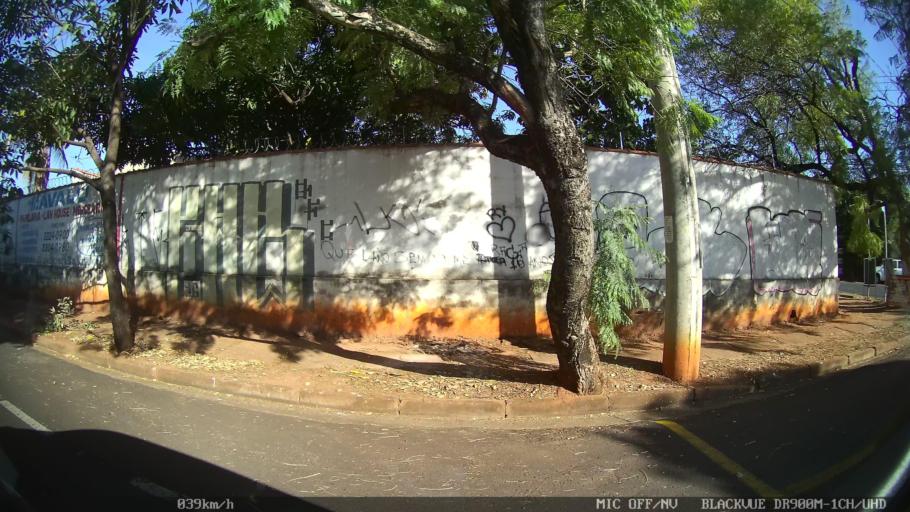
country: BR
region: Sao Paulo
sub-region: Sao Jose Do Rio Preto
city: Sao Jose do Rio Preto
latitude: -20.7802
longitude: -49.3652
